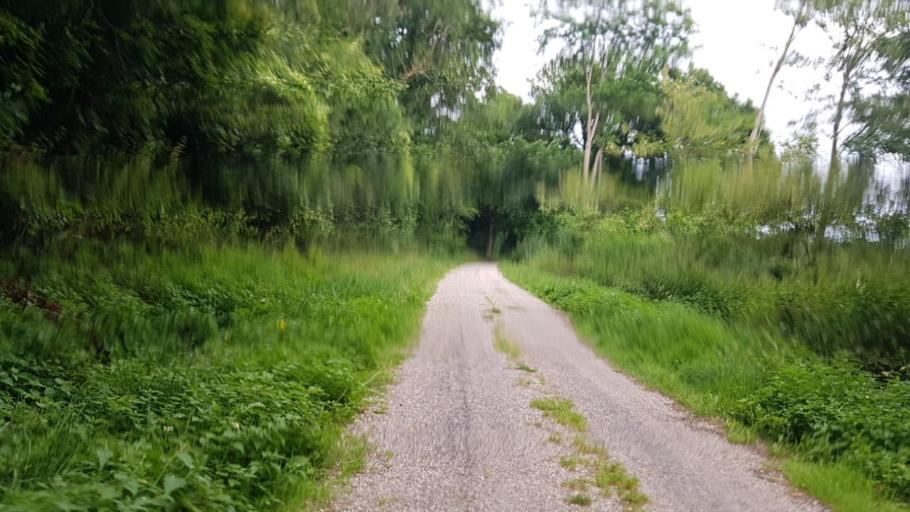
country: FR
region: Picardie
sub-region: Departement de l'Aisne
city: Origny-en-Thierache
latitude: 49.9320
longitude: 4.0066
